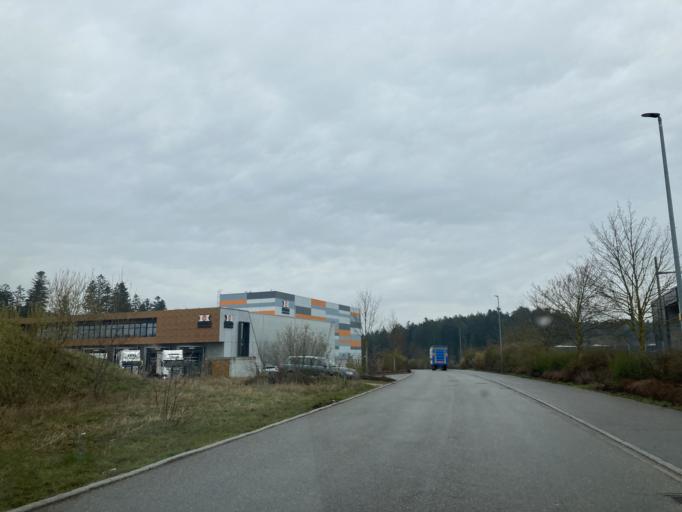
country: DE
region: Baden-Wuerttemberg
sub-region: Freiburg Region
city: Aichhalden
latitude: 48.2408
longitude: 8.4212
